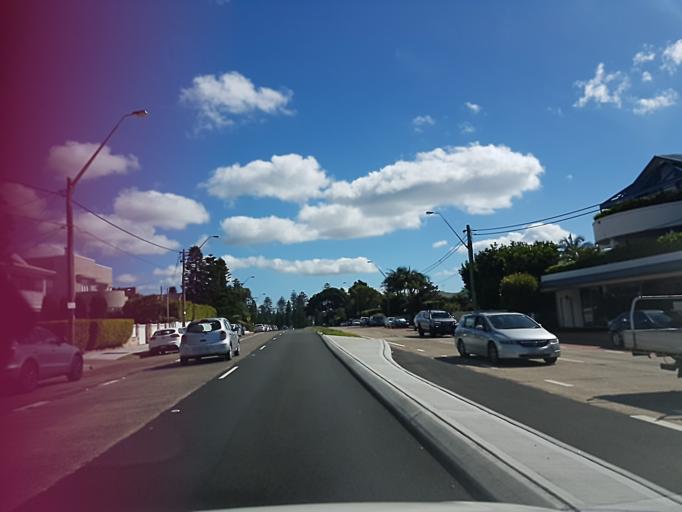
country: AU
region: New South Wales
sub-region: Warringah
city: Dee Why
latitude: -33.7367
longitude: 151.3024
